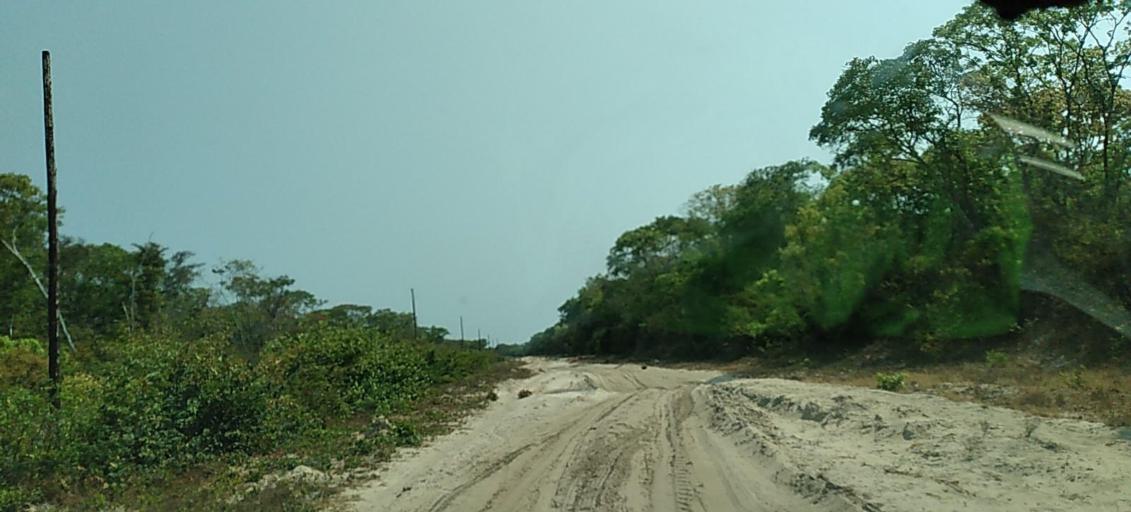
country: ZM
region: North-Western
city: Kabompo
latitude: -13.2794
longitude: 24.0592
